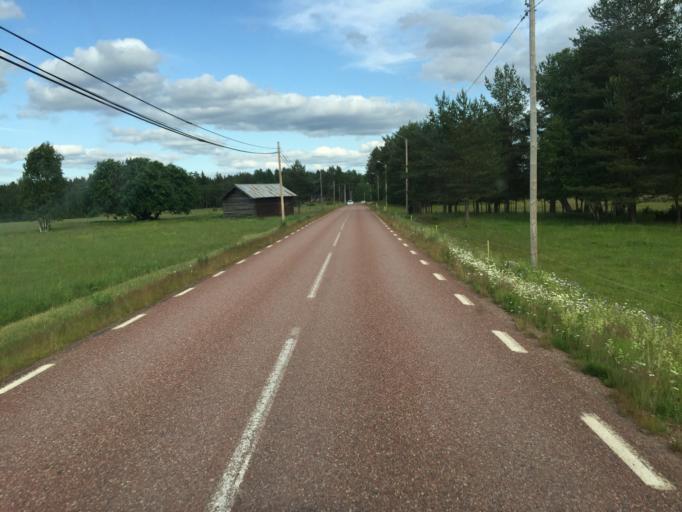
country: SE
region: Dalarna
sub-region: Alvdalens Kommun
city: AElvdalen
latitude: 60.9548
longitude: 13.9231
